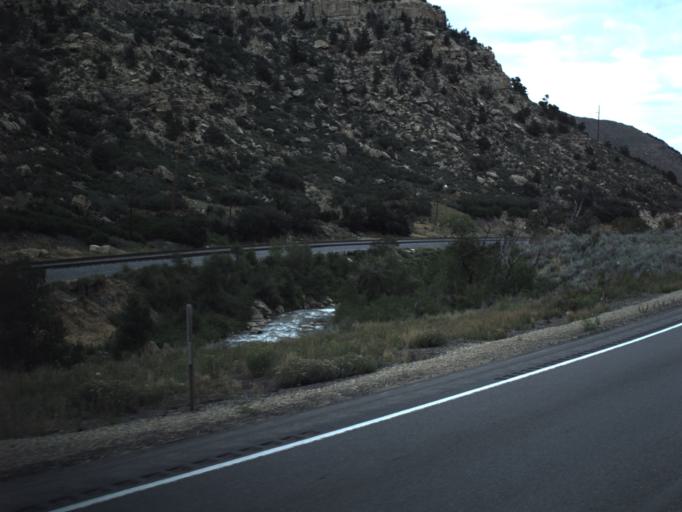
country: US
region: Utah
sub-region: Carbon County
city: Helper
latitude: 39.7908
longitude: -110.9313
